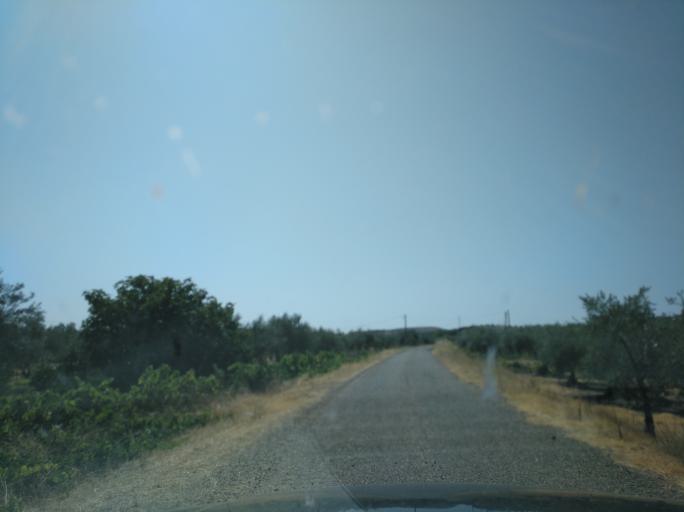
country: PT
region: Portalegre
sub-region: Campo Maior
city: Campo Maior
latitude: 39.0746
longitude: -7.0176
